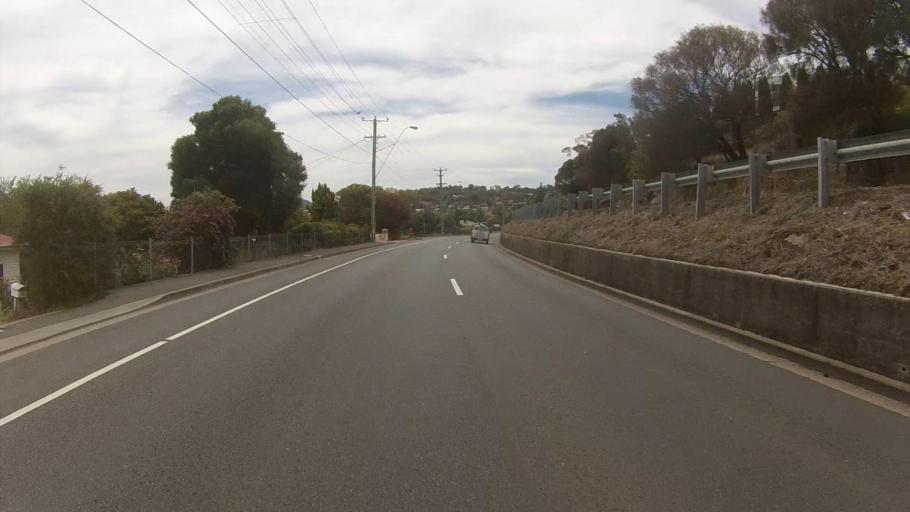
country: AU
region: Tasmania
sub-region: Clarence
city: Lindisfarne
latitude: -42.8549
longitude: 147.3567
